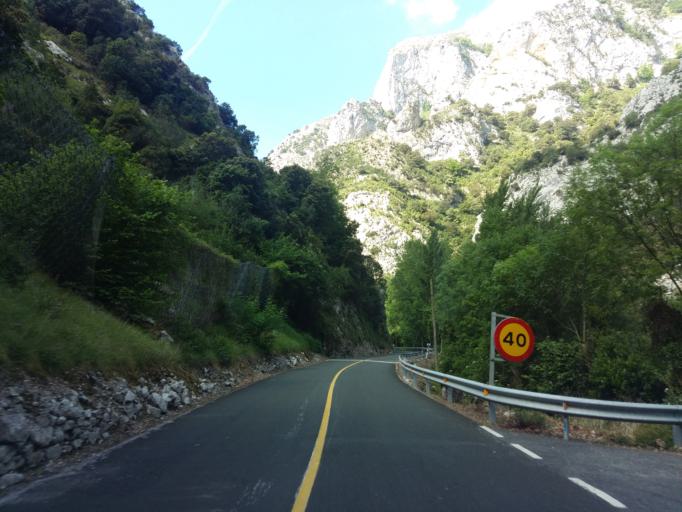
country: ES
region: Cantabria
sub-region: Provincia de Cantabria
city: Potes
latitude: 43.2323
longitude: -4.5793
